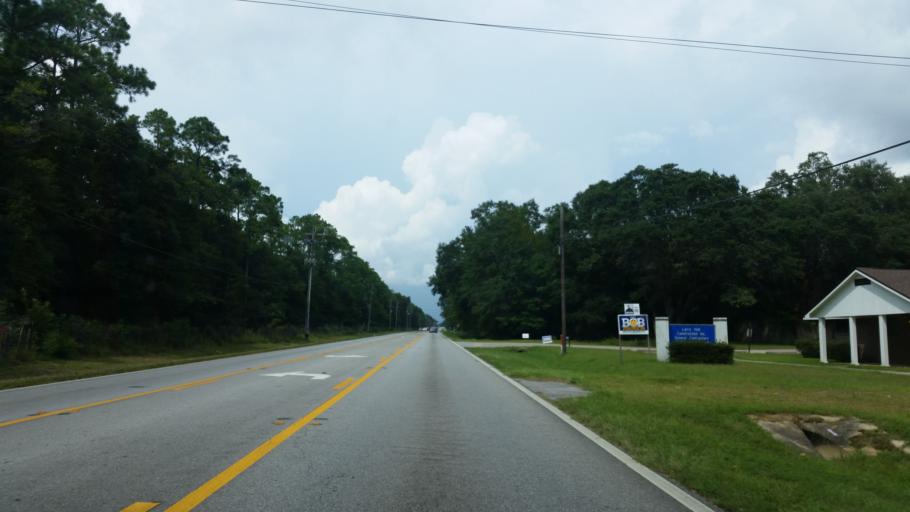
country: US
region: Florida
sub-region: Santa Rosa County
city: Pace
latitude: 30.6091
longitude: -87.1822
